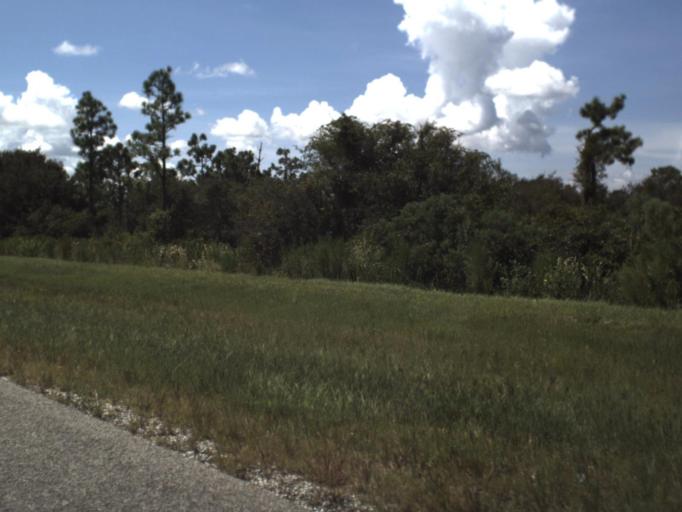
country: US
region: Florida
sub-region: Charlotte County
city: Harbour Heights
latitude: 27.0206
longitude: -81.9587
